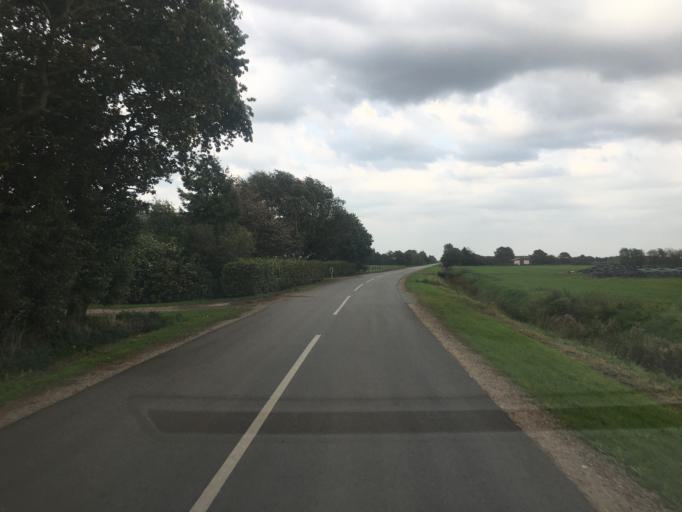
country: DK
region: South Denmark
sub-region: Tonder Kommune
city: Logumkloster
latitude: 55.0629
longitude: 9.0249
